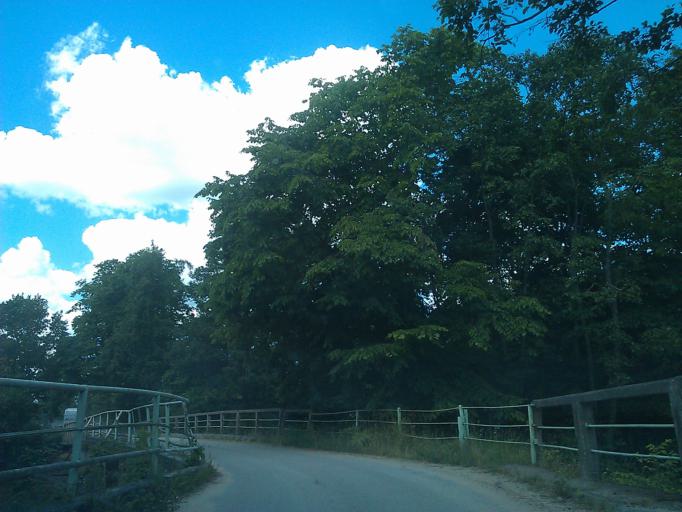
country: LV
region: Vilanu
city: Vilani
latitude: 56.5891
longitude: 26.9513
